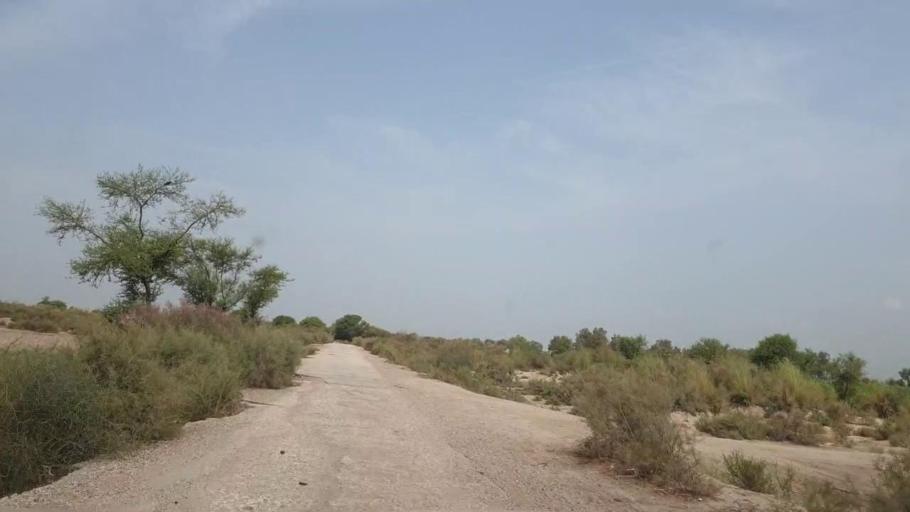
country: PK
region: Sindh
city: Sobhadero
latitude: 27.3939
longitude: 68.2635
